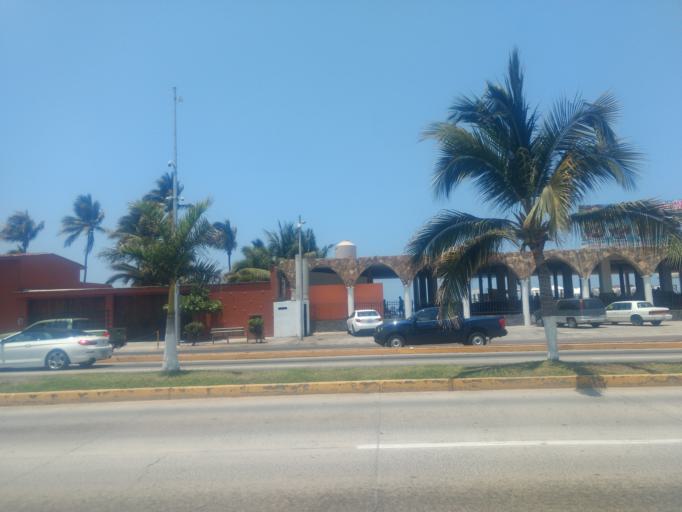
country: MX
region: Colima
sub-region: Manzanillo
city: Manzanillo
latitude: 19.0954
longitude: -104.3193
